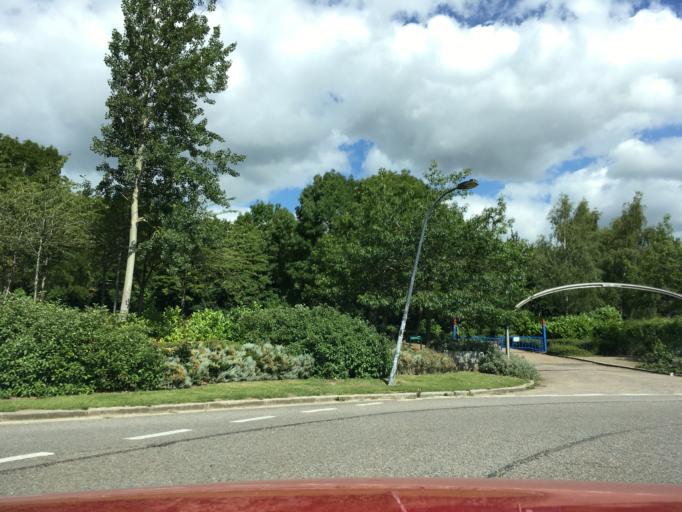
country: GB
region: England
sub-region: Milton Keynes
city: Milton Keynes
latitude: 52.0469
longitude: -0.7371
